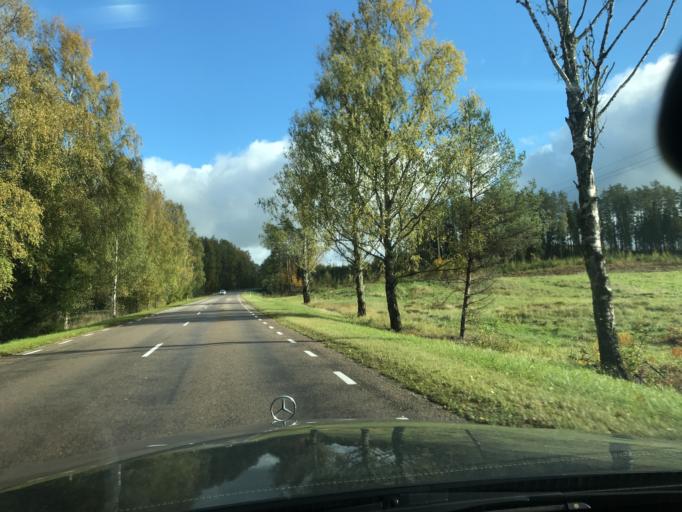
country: EE
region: Valgamaa
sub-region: Torva linn
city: Torva
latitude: 57.9877
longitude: 26.0553
